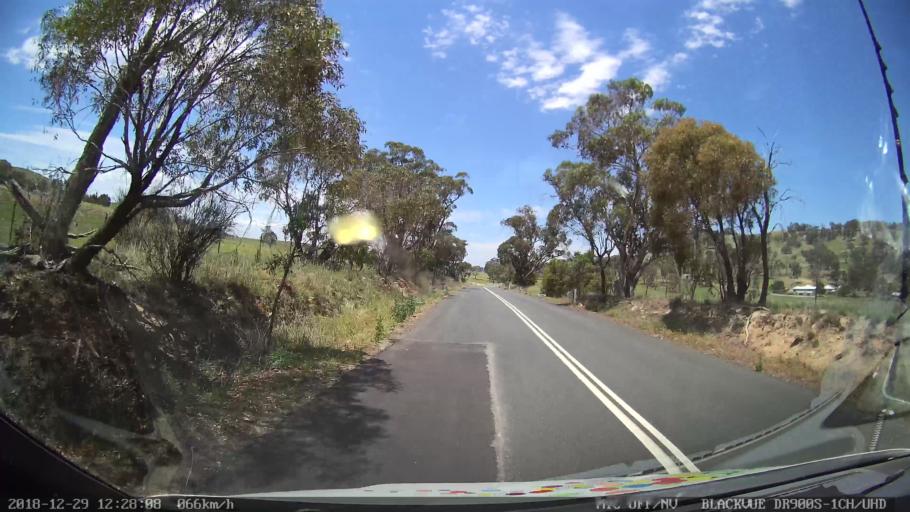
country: AU
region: Australian Capital Territory
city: Macarthur
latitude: -35.4833
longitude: 149.2253
